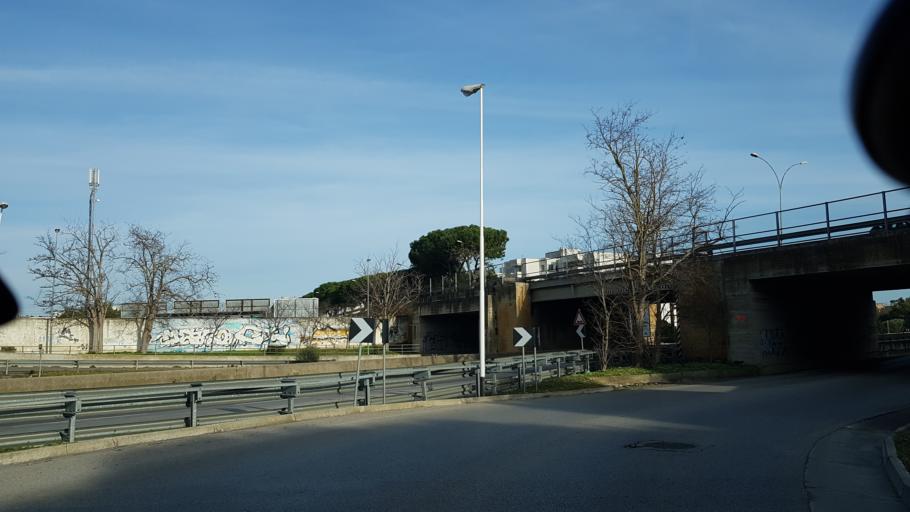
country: IT
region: Apulia
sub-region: Provincia di Brindisi
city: Brindisi
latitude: 40.6227
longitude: 17.9235
